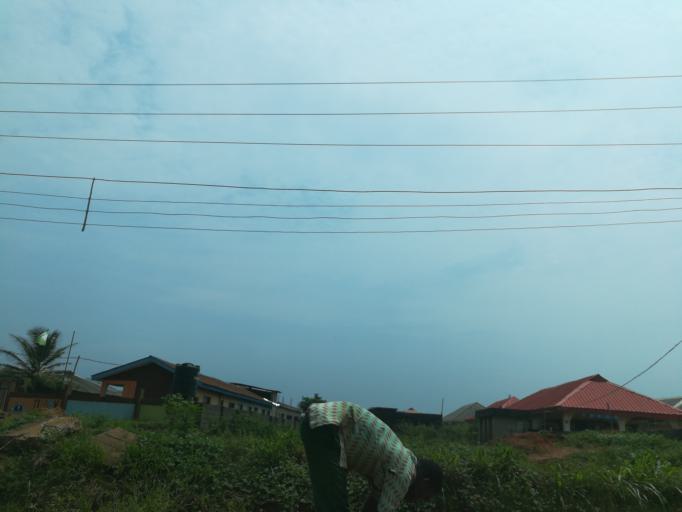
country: NG
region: Lagos
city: Ikorodu
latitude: 6.6047
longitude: 3.6010
